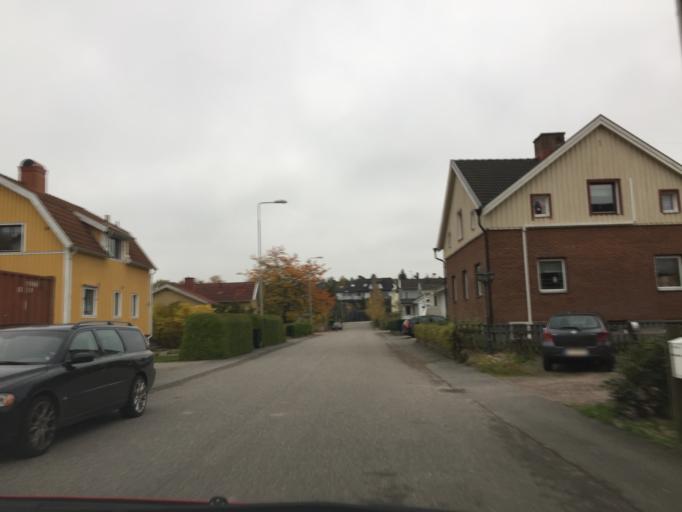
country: SE
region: Vaestra Goetaland
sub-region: Trollhattan
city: Trollhattan
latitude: 58.2659
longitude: 12.2739
